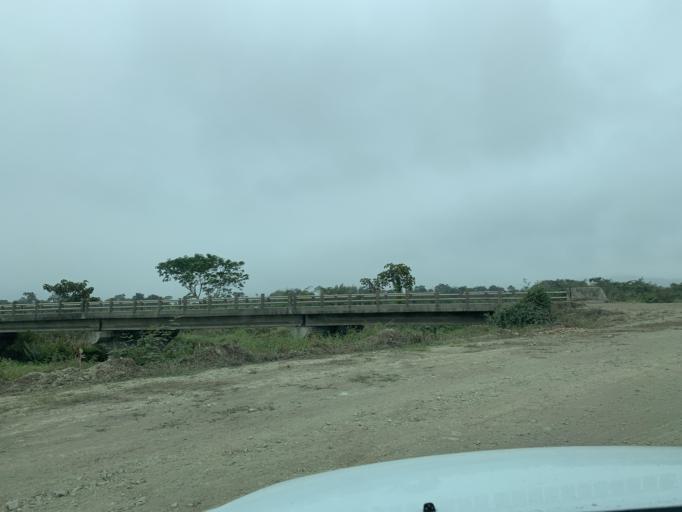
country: EC
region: Guayas
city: Coronel Marcelino Mariduena
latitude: -2.3575
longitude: -79.5839
